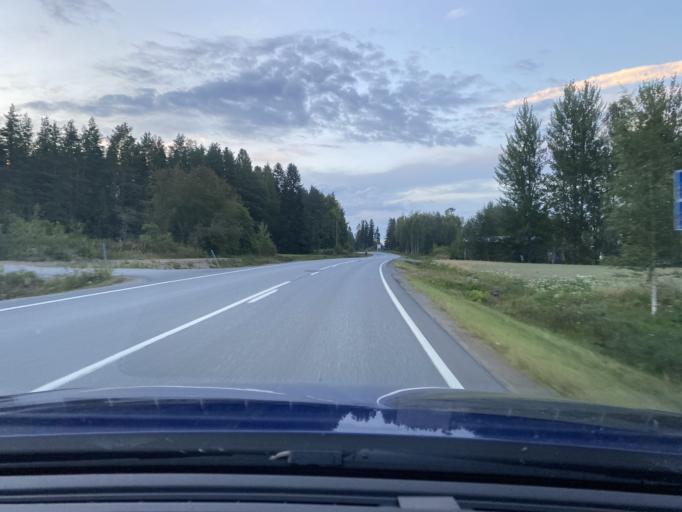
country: FI
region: Satakunta
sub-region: Pohjois-Satakunta
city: Honkajoki
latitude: 62.0762
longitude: 22.2494
